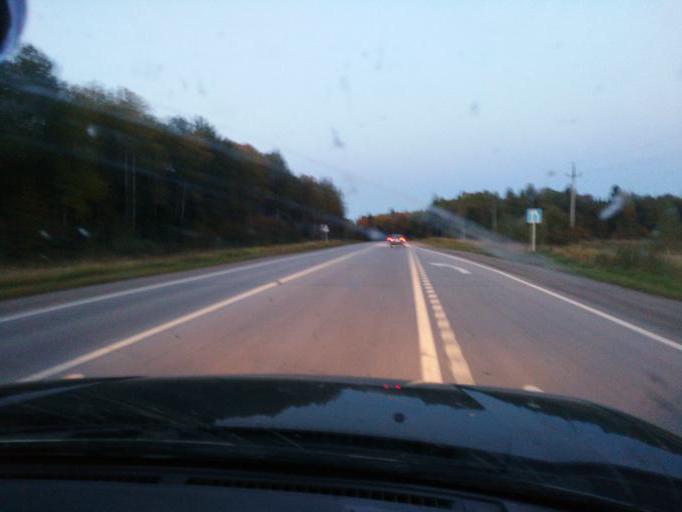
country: RU
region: Perm
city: Kalino
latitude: 58.2688
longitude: 57.3597
